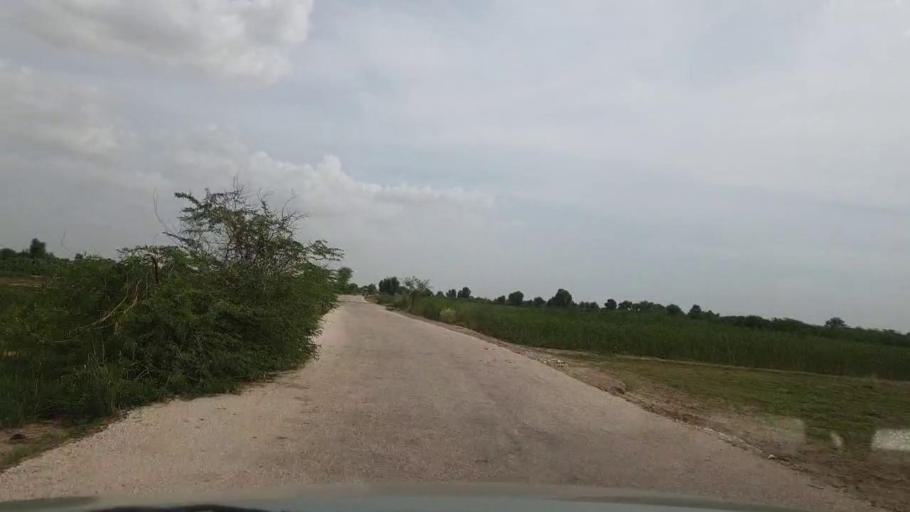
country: PK
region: Sindh
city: Kot Diji
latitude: 27.1448
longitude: 69.0281
